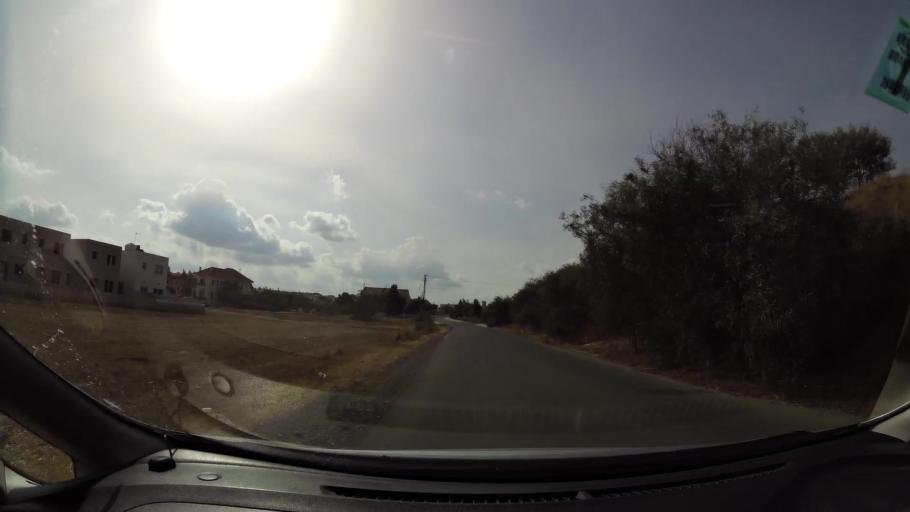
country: CY
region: Lefkosia
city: Geri
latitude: 35.0660
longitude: 33.3950
